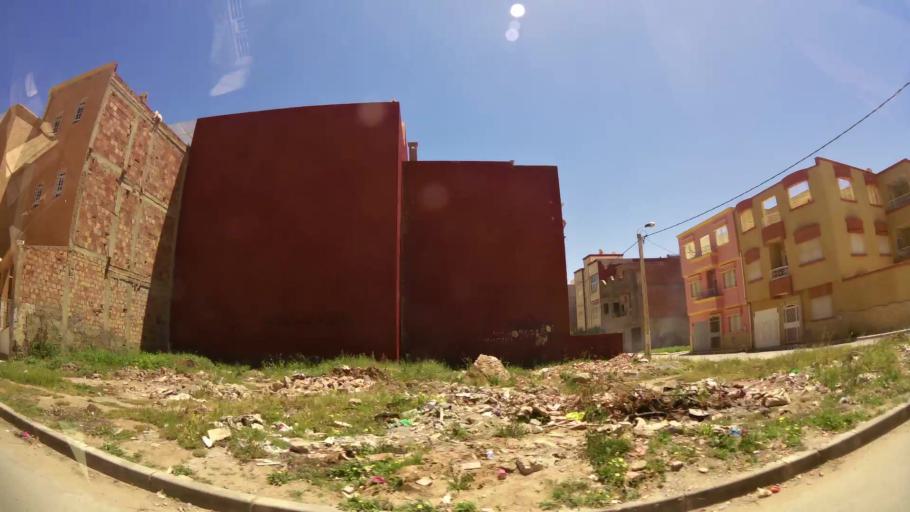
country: MA
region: Oriental
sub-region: Berkane-Taourirt
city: Madagh
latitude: 35.0808
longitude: -2.2280
